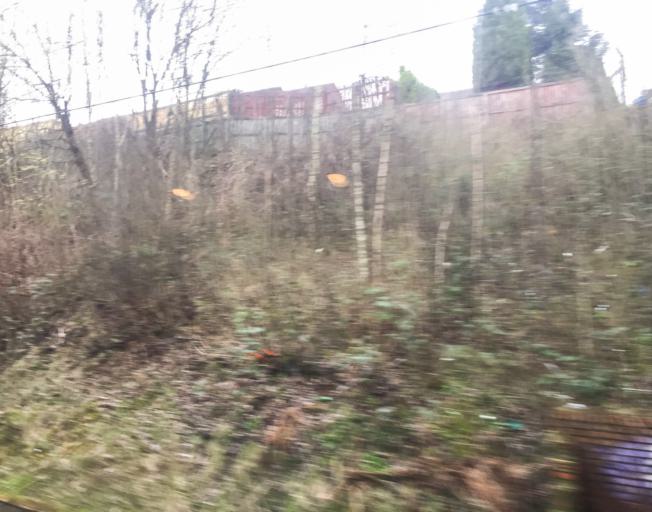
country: GB
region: Scotland
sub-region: West Dunbartonshire
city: Old Kilpatrick
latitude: 55.9203
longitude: -4.4464
